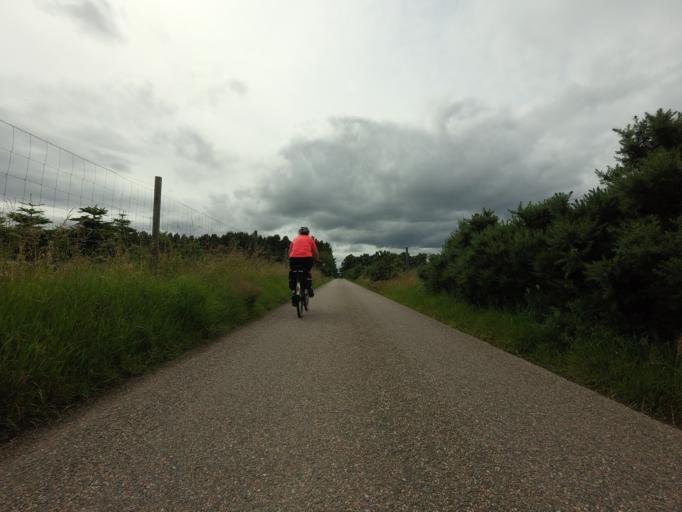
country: GB
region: Scotland
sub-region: Highland
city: Nairn
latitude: 57.6043
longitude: -3.7619
